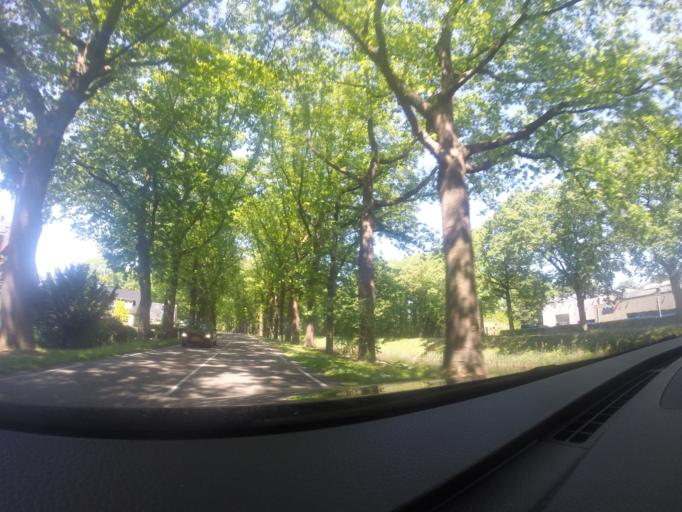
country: NL
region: Gelderland
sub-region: Gemeente Brummen
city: Eerbeek
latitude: 52.1054
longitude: 6.0855
